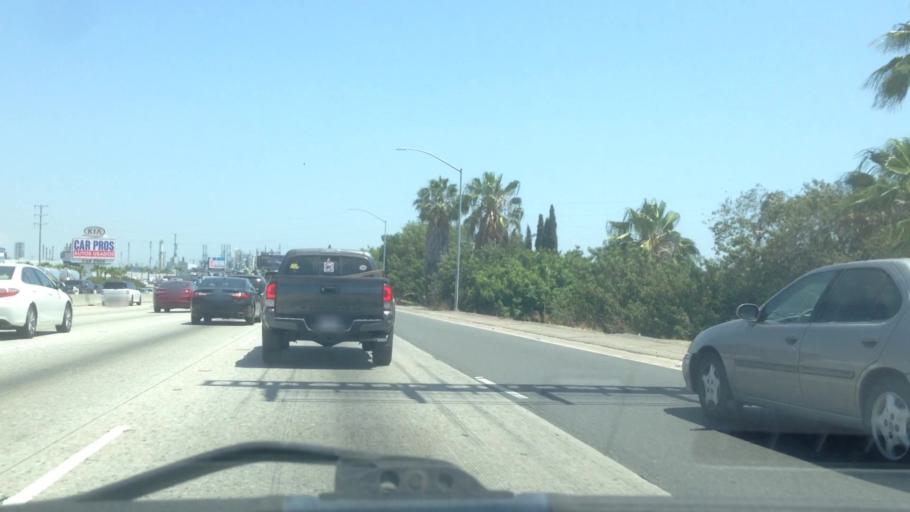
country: US
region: California
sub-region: Los Angeles County
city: Carson
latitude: 33.8292
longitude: -118.2537
